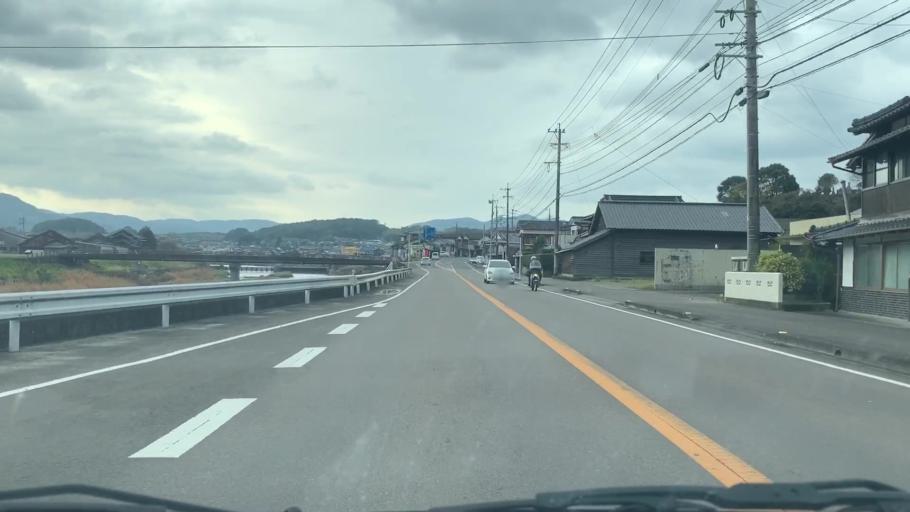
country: JP
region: Saga Prefecture
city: Ureshinomachi-shimojuku
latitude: 33.1298
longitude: 130.0067
